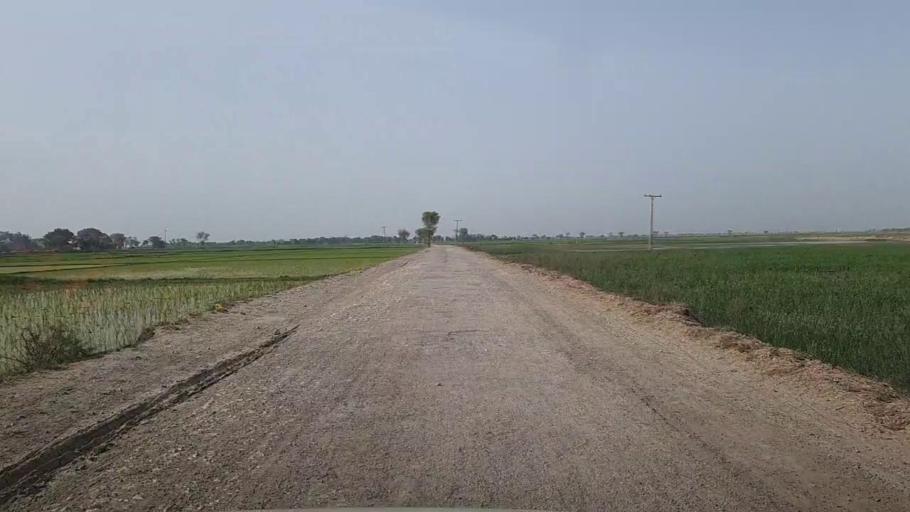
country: PK
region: Sindh
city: Mehar
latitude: 27.1124
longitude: 67.8199
